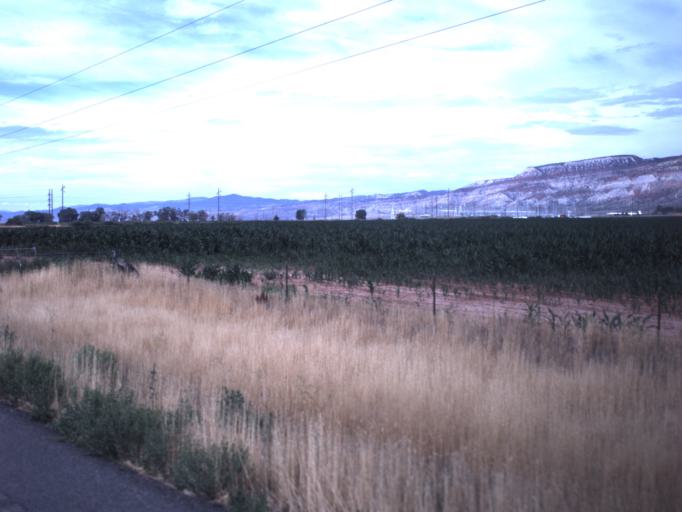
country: US
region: Utah
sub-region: Sevier County
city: Aurora
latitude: 38.8482
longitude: -111.9775
